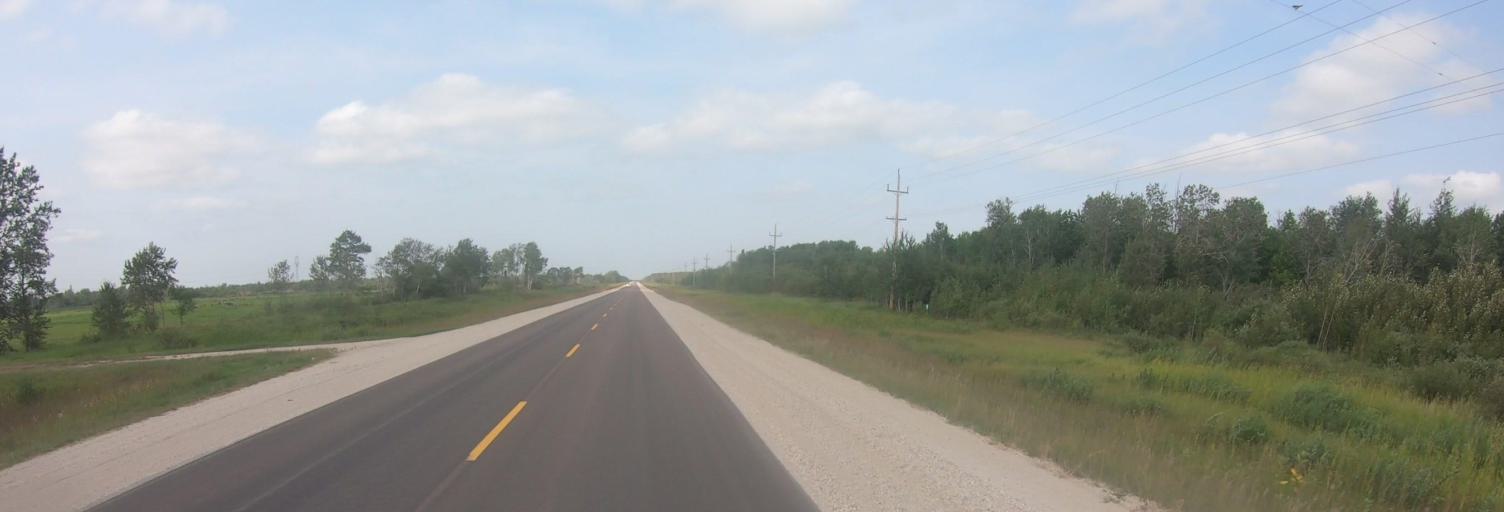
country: CA
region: Manitoba
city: La Broquerie
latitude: 49.2670
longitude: -96.3990
